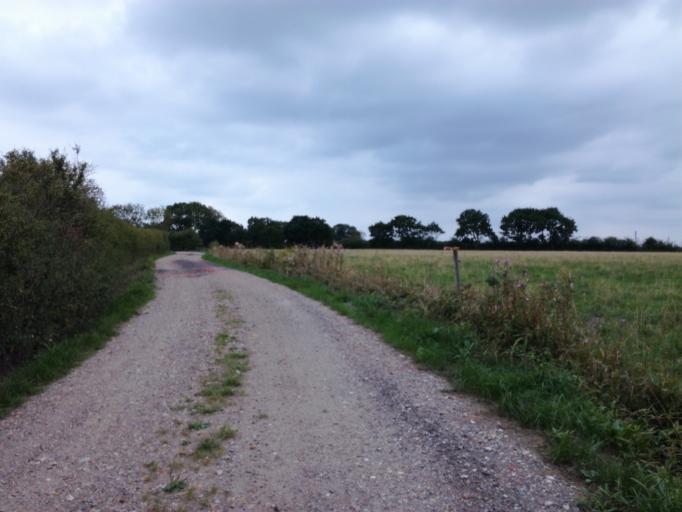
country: DK
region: South Denmark
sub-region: Fredericia Kommune
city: Fredericia
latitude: 55.6073
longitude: 9.7866
